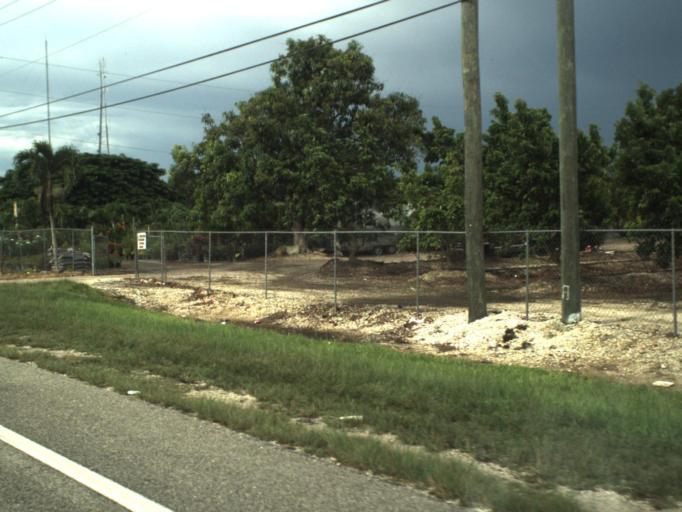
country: US
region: Florida
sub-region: Miami-Dade County
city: Homestead
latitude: 25.5152
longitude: -80.4778
